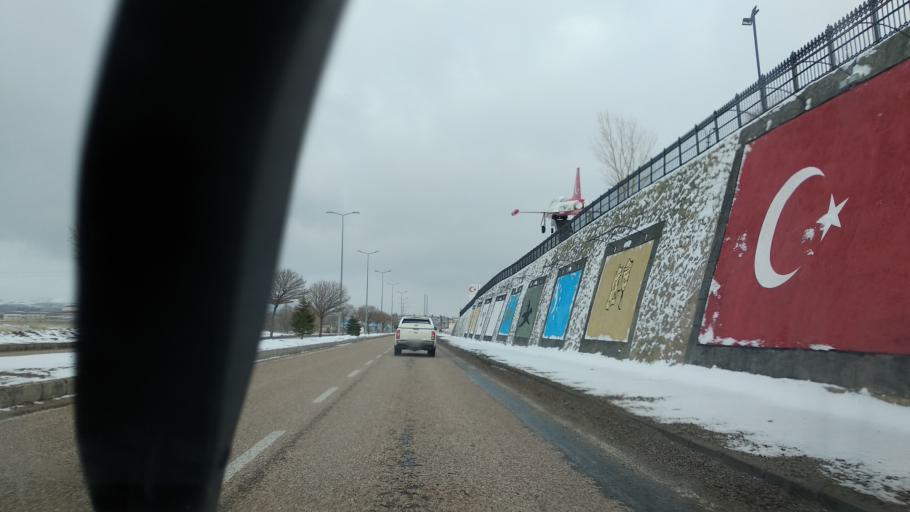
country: TR
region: Kayseri
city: Pinarbasi
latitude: 38.7114
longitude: 36.3779
